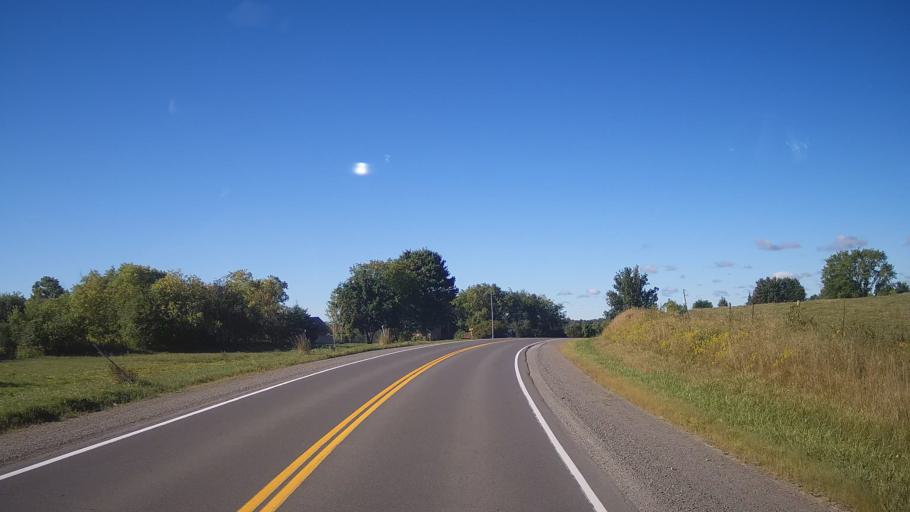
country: CA
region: Ontario
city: Bells Corners
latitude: 45.0962
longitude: -75.6159
